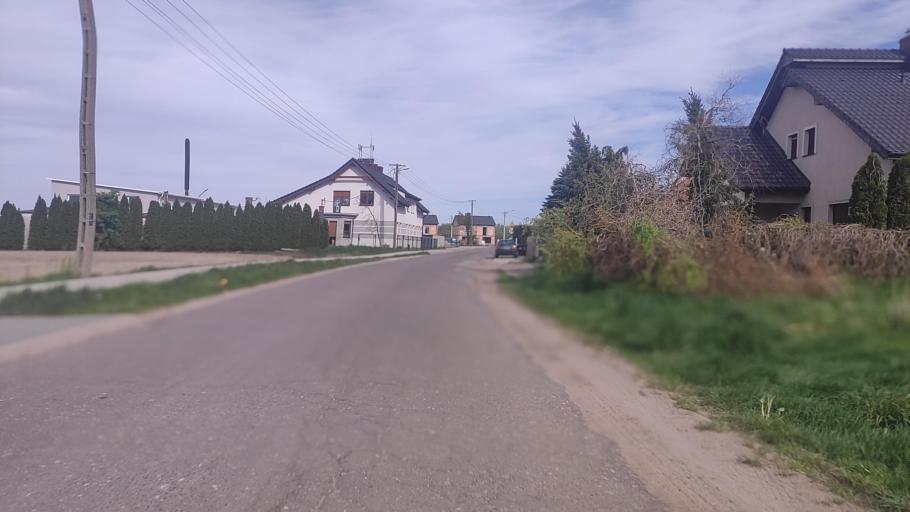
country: PL
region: Greater Poland Voivodeship
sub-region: Powiat poznanski
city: Kleszczewo
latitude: 52.3846
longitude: 17.1512
